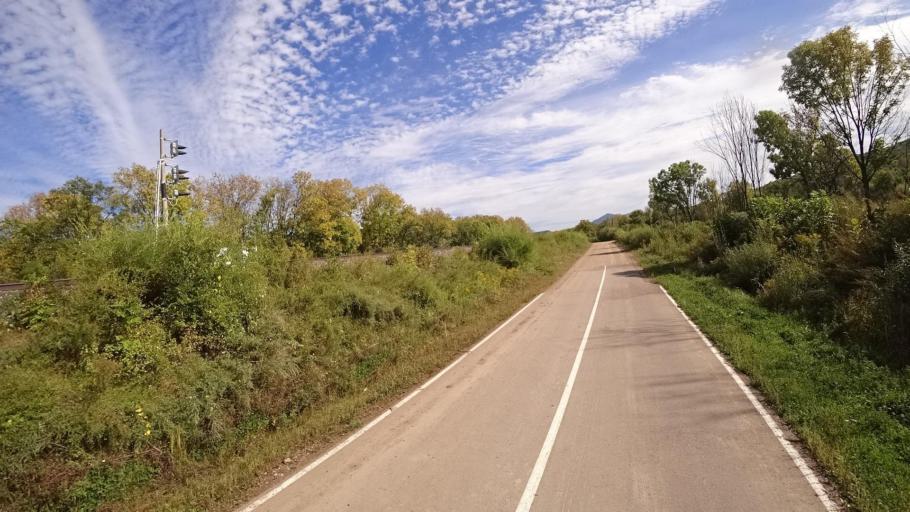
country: RU
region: Primorskiy
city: Yakovlevka
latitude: 44.3925
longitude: 133.6079
